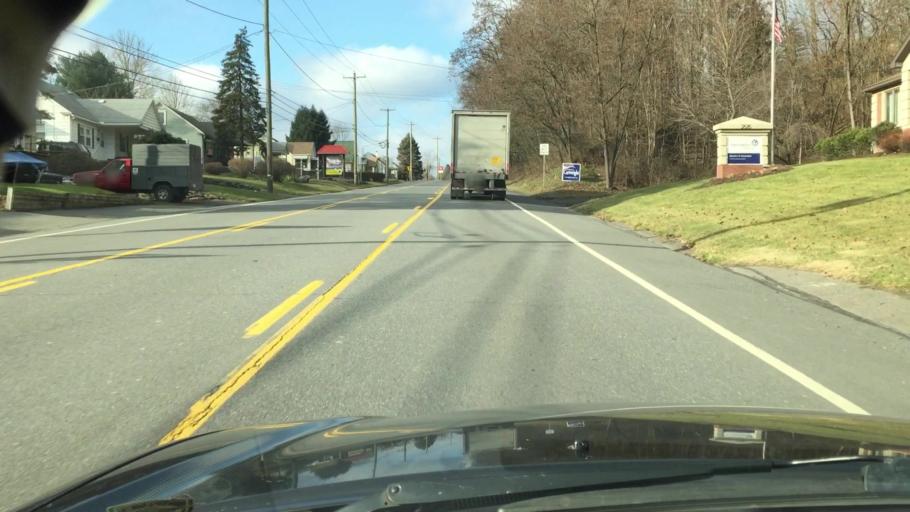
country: US
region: Pennsylvania
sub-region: Luzerne County
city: Dallas
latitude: 41.3345
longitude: -75.9565
